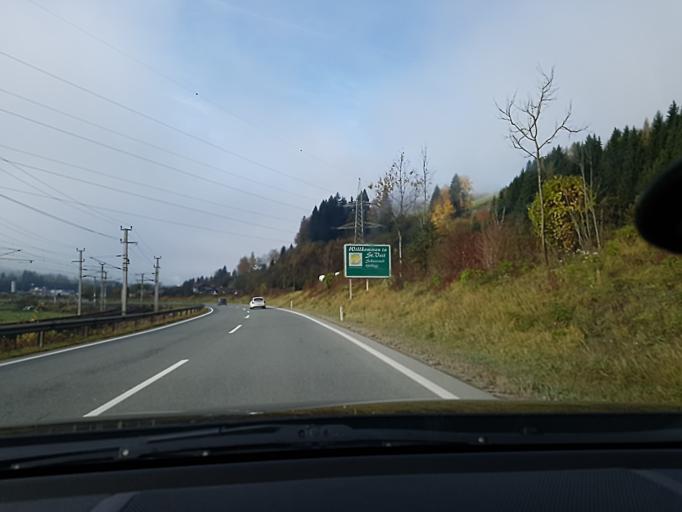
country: AT
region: Salzburg
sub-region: Politischer Bezirk Sankt Johann im Pongau
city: Sankt Johann im Pongau
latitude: 47.3283
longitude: 13.1816
